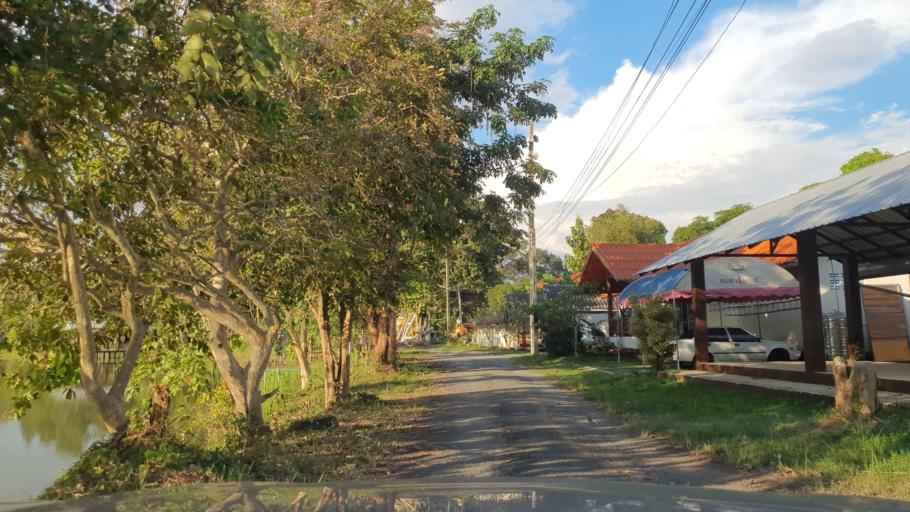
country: TH
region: Chiang Mai
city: San Sai
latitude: 18.8738
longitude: 99.1584
